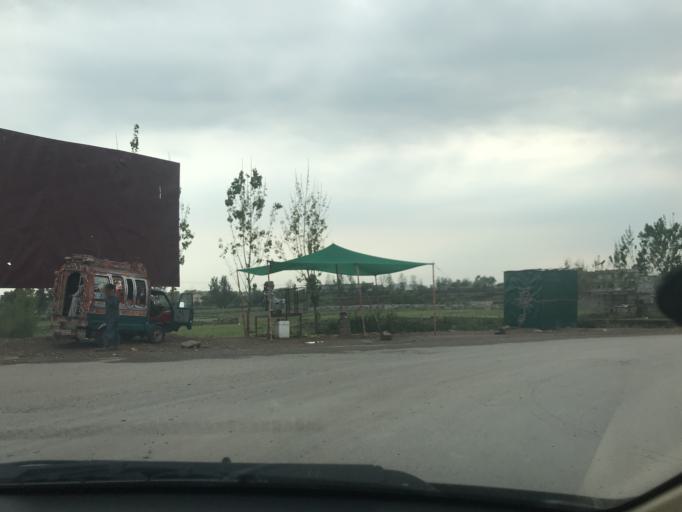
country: PK
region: Islamabad
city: Islamabad
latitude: 33.6885
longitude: 73.1729
